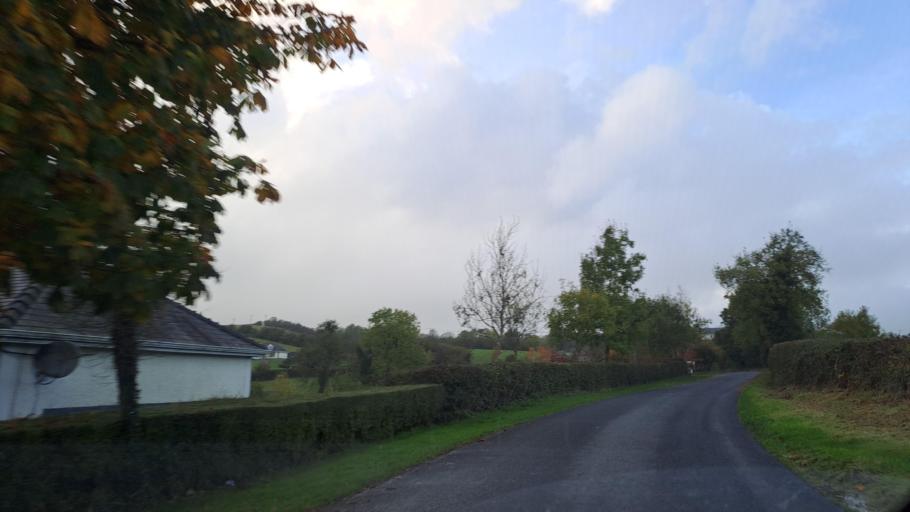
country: IE
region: Ulster
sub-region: An Cabhan
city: Kingscourt
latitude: 53.9688
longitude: -6.7860
